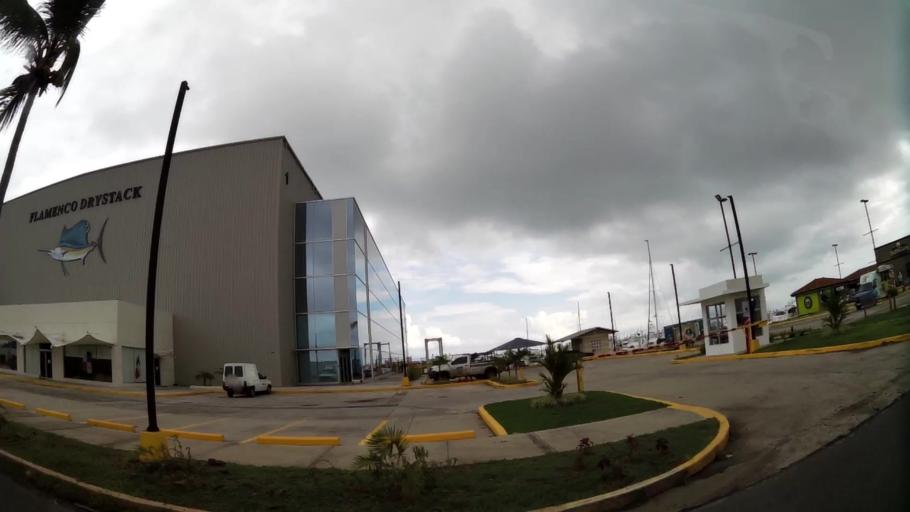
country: PA
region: Panama
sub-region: Distrito de Panama
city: Ancon
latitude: 8.9116
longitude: -79.5235
